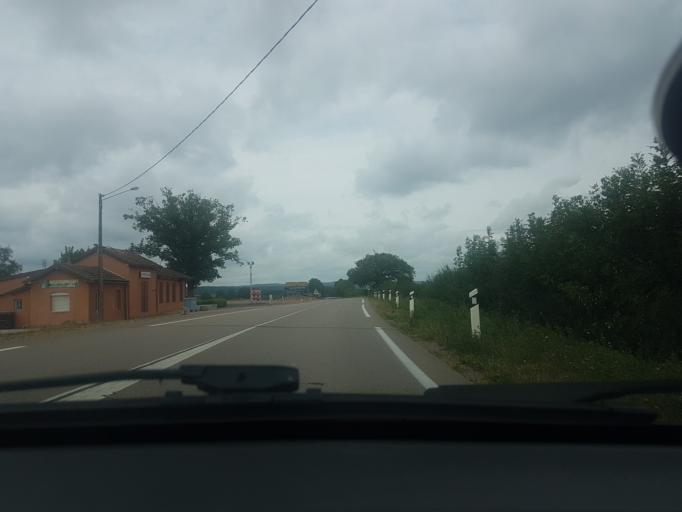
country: FR
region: Bourgogne
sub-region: Departement de la Cote-d'Or
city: Saulieu
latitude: 47.2264
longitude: 4.3183
